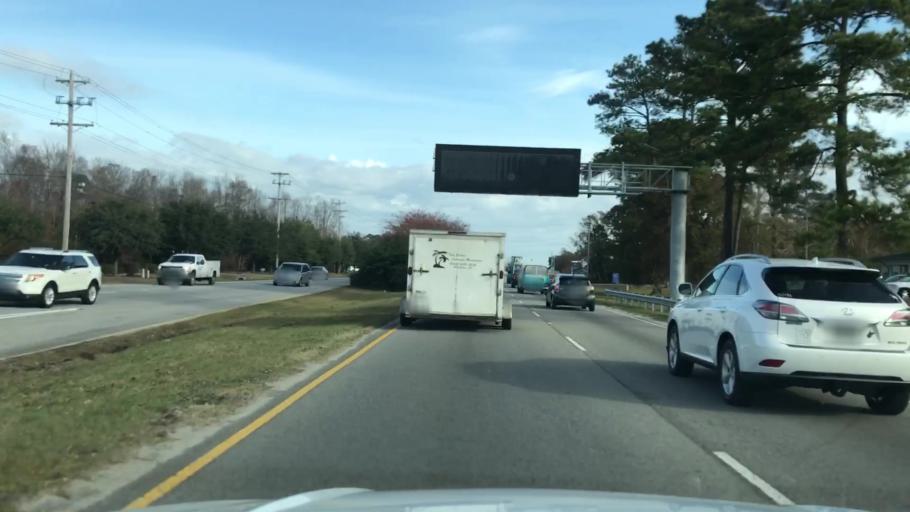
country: US
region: South Carolina
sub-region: Georgetown County
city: Murrells Inlet
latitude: 33.5563
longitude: -79.0437
